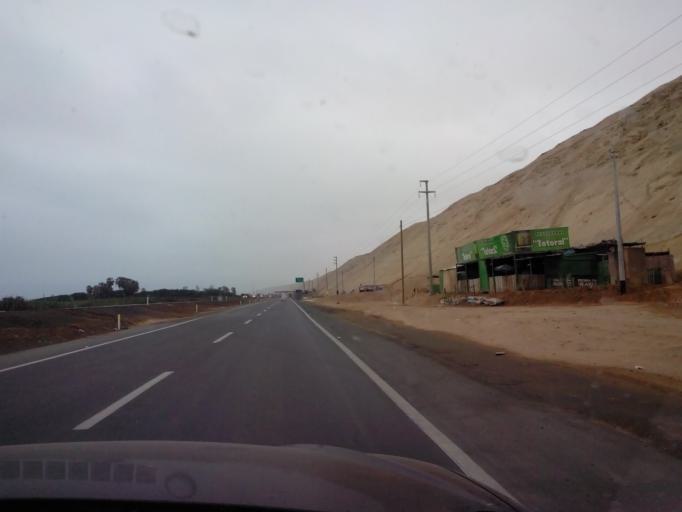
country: PE
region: Ica
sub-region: Provincia de Chincha
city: San Pedro
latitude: -13.3928
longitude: -76.1989
